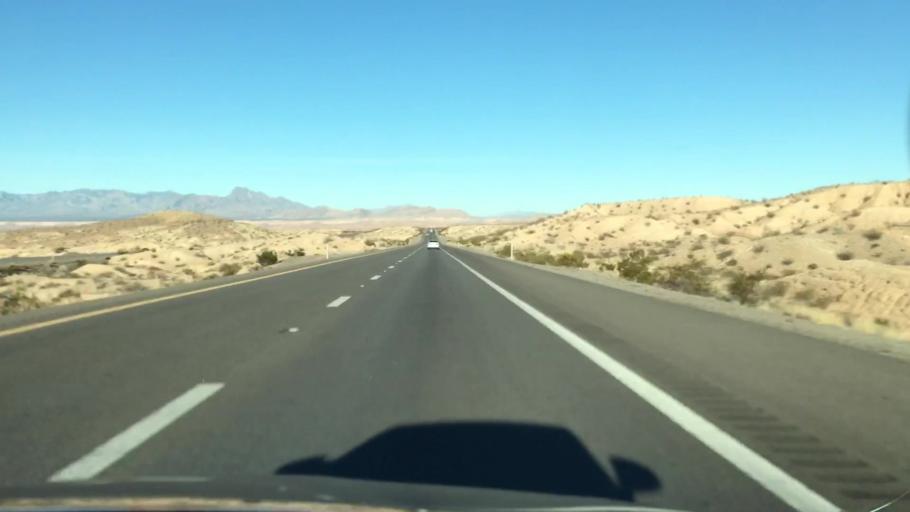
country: US
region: Nevada
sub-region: Clark County
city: Moapa Town
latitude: 36.6028
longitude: -114.6370
